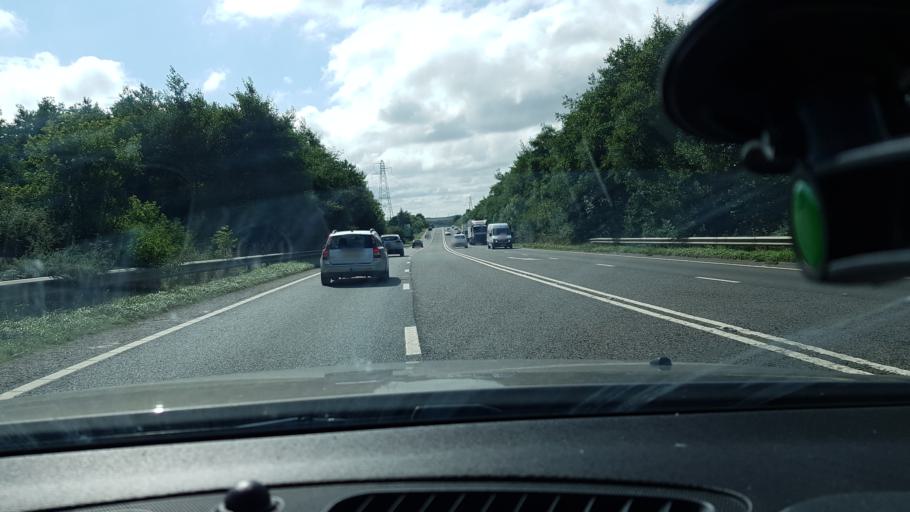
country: GB
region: England
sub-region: Cornwall
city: Truro
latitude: 50.3174
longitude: -5.0819
